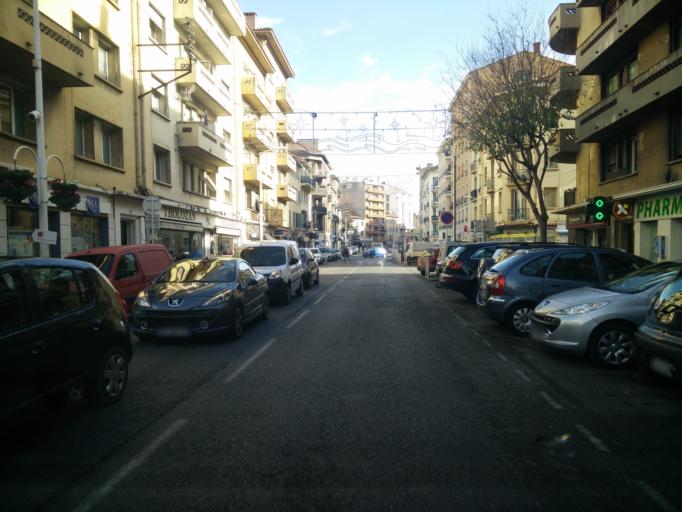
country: FR
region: Provence-Alpes-Cote d'Azur
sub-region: Departement du Var
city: Toulon
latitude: 43.1286
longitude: 5.9138
